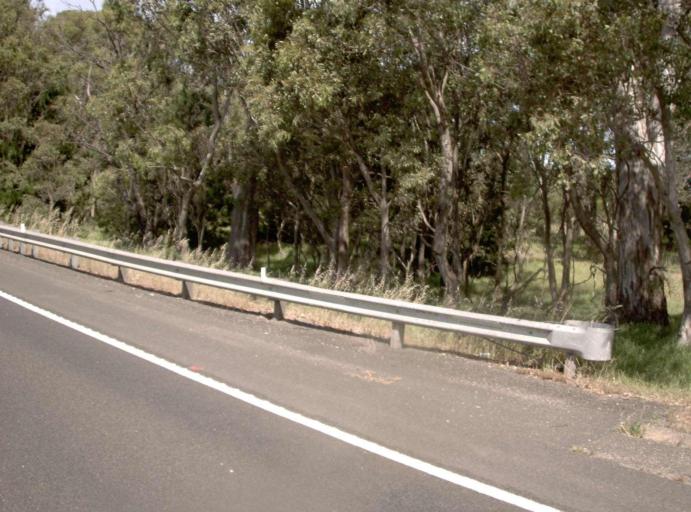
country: AU
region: Victoria
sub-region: East Gippsland
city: Bairnsdale
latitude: -37.8767
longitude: 147.4418
